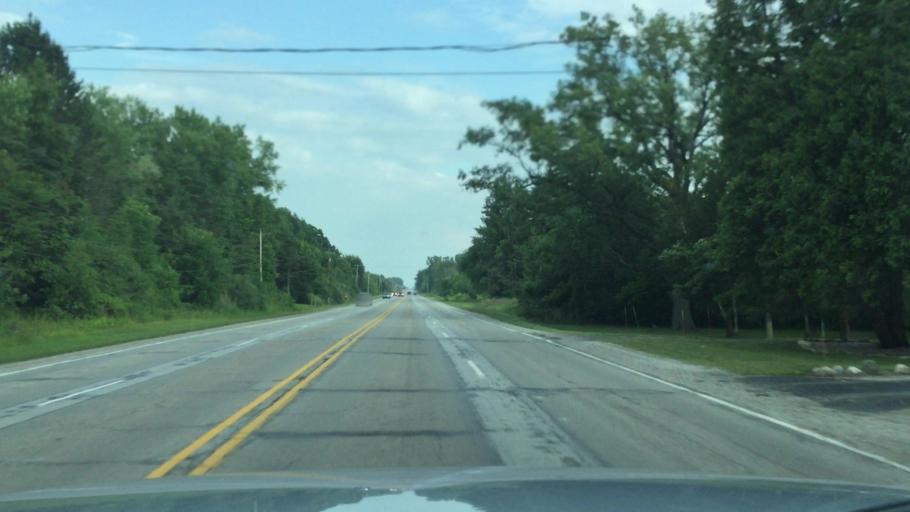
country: US
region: Michigan
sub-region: Saginaw County
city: Birch Run
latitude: 43.2766
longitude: -83.7893
